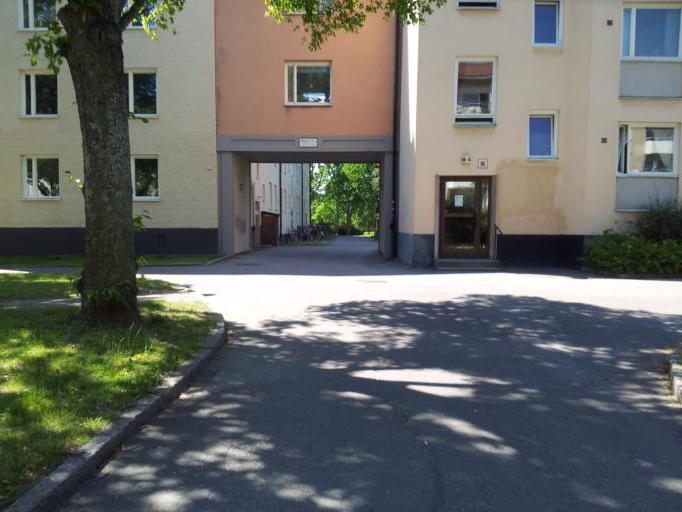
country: SE
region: Uppsala
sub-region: Uppsala Kommun
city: Uppsala
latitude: 59.8684
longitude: 17.6773
